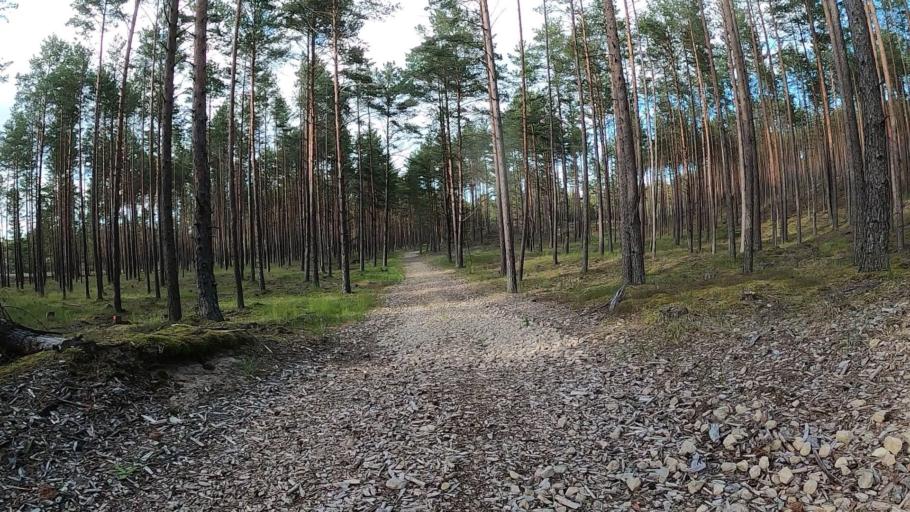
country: LV
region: Riga
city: Jaunciems
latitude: 57.0577
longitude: 24.1254
